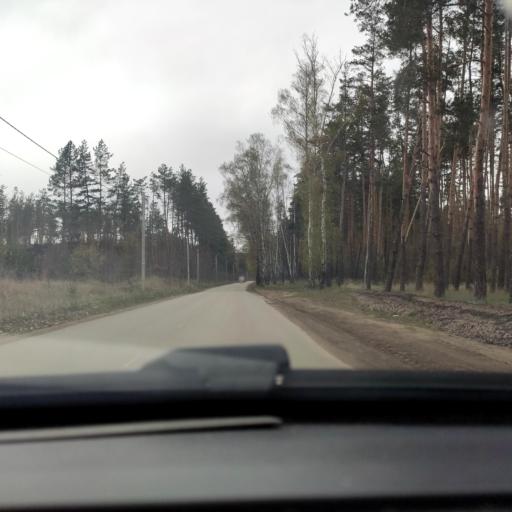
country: RU
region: Voronezj
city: Podgornoye
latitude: 51.7474
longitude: 39.1604
